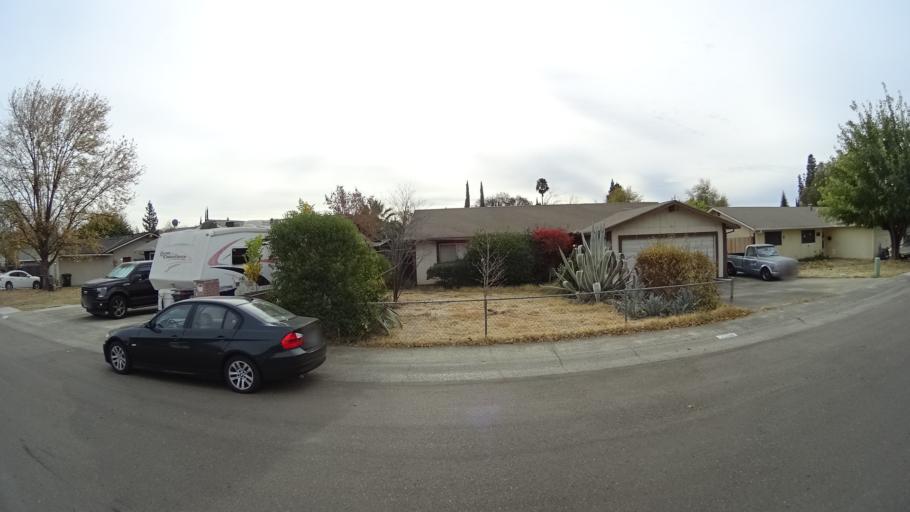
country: US
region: California
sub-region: Sacramento County
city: Citrus Heights
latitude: 38.7163
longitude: -121.2959
